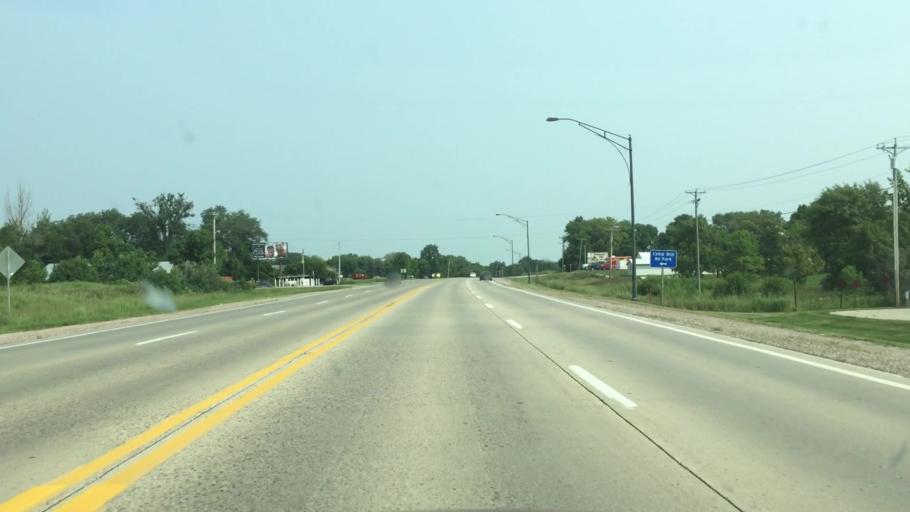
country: US
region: Iowa
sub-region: Dickinson County
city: Arnolds Park
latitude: 43.3559
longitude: -95.1421
